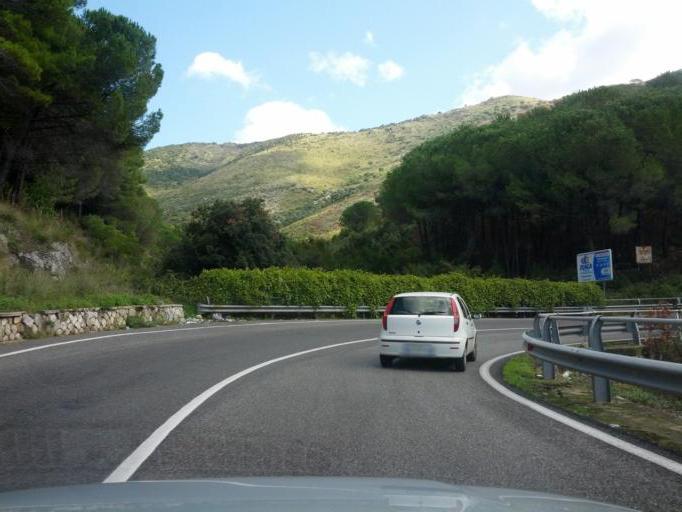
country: IT
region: Latium
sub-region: Provincia di Latina
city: Itri
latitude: 41.3147
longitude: 13.4915
